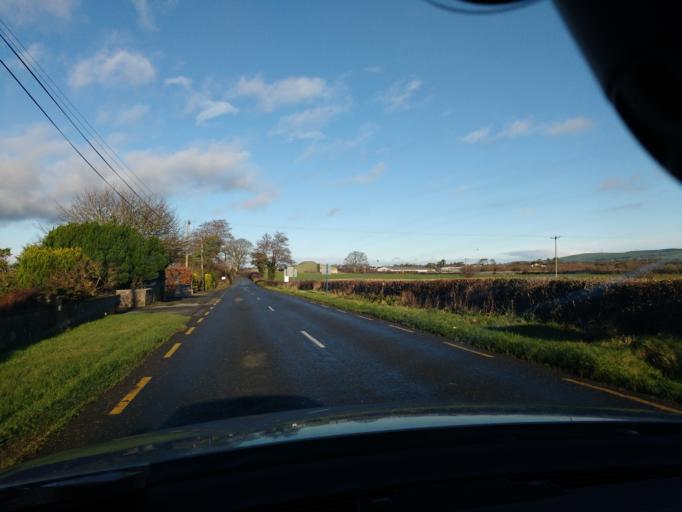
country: IE
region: Leinster
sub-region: Laois
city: Rathdowney
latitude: 52.7115
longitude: -7.5841
